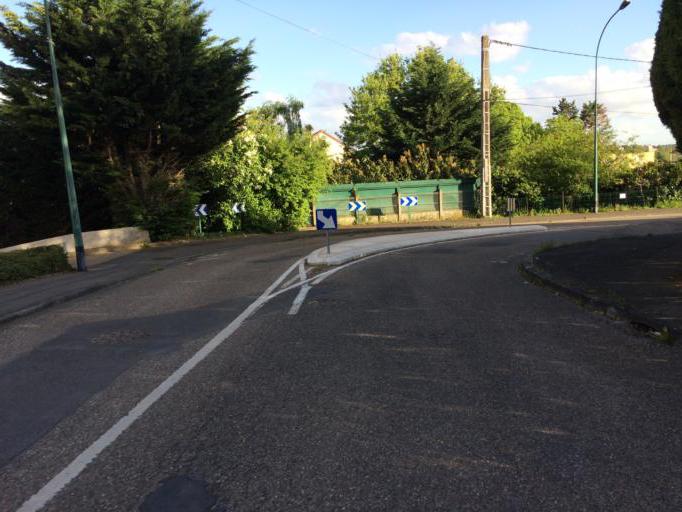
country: FR
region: Ile-de-France
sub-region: Departement de l'Essonne
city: Verrieres-le-Buisson
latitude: 48.7456
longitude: 2.2758
